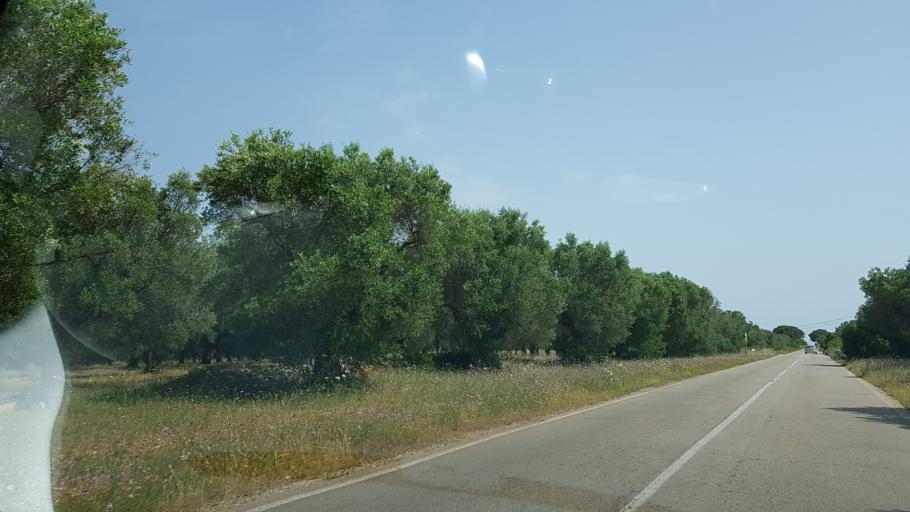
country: IT
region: Apulia
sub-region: Provincia di Brindisi
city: San Pancrazio Salentino
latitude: 40.3488
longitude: 17.8463
